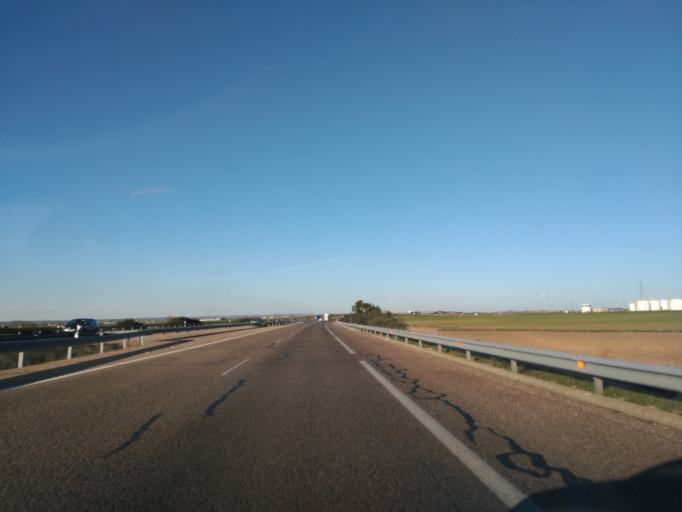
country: ES
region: Castille and Leon
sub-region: Provincia de Salamanca
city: Castellanos de Moriscos
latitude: 41.0218
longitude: -5.5797
